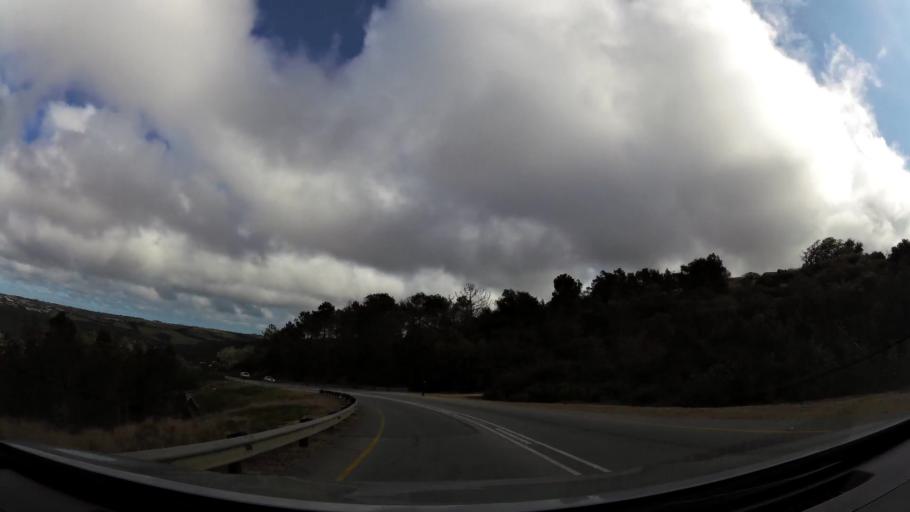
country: ZA
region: Western Cape
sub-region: Eden District Municipality
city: Plettenberg Bay
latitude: -34.0535
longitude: 23.3525
